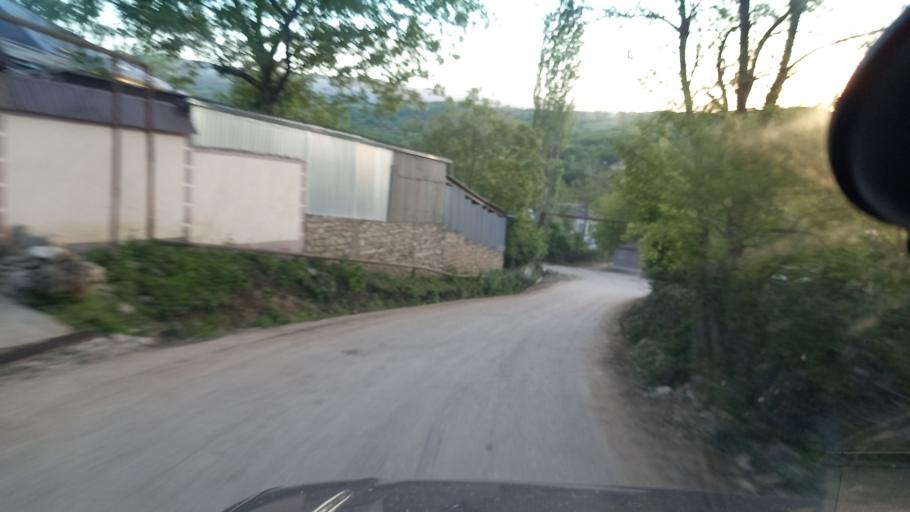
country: RU
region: Dagestan
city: Khuchni
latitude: 42.0263
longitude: 47.9669
